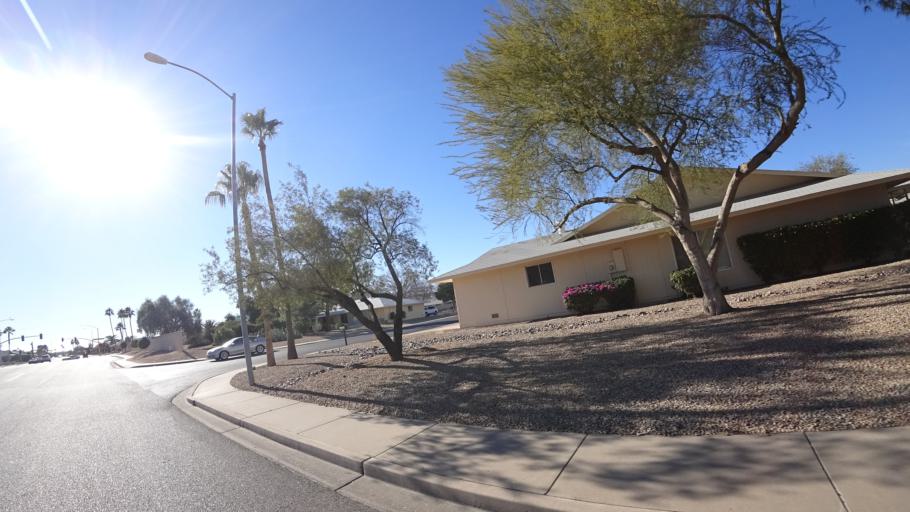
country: US
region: Arizona
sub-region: Maricopa County
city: Sun City West
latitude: 33.6506
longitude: -112.3365
